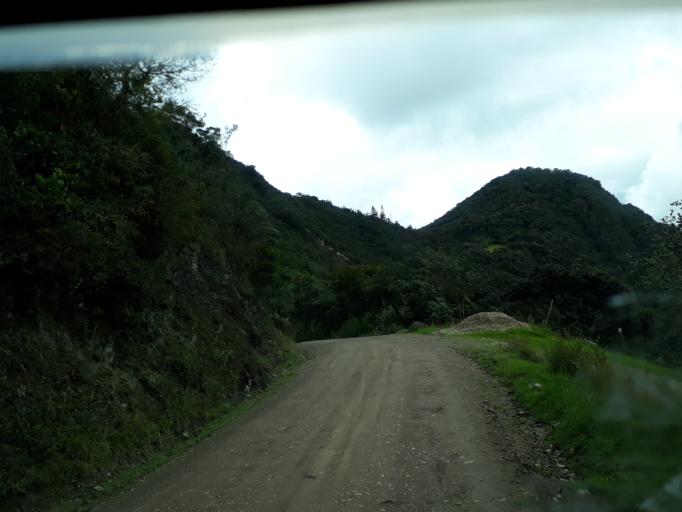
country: CO
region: Cundinamarca
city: Cogua
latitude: 5.1593
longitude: -73.9871
